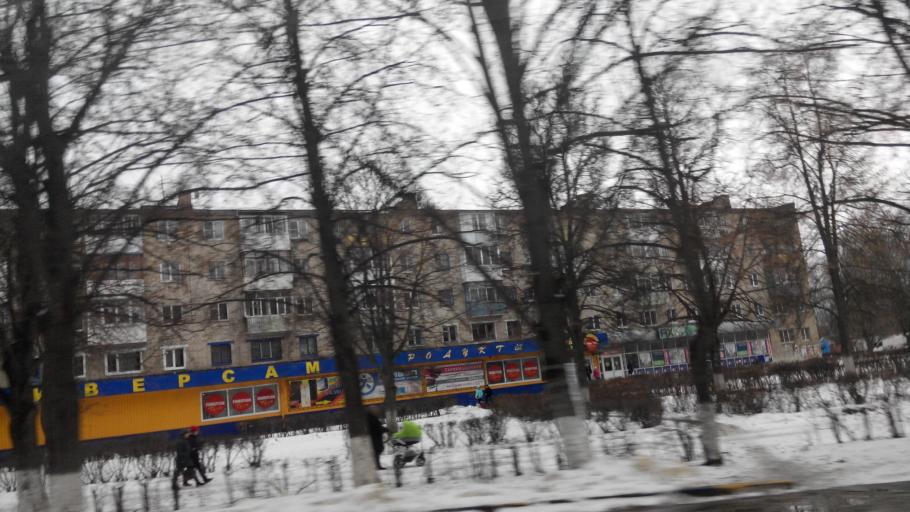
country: RU
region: Tula
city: Uzlovaya
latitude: 53.9734
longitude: 38.1841
